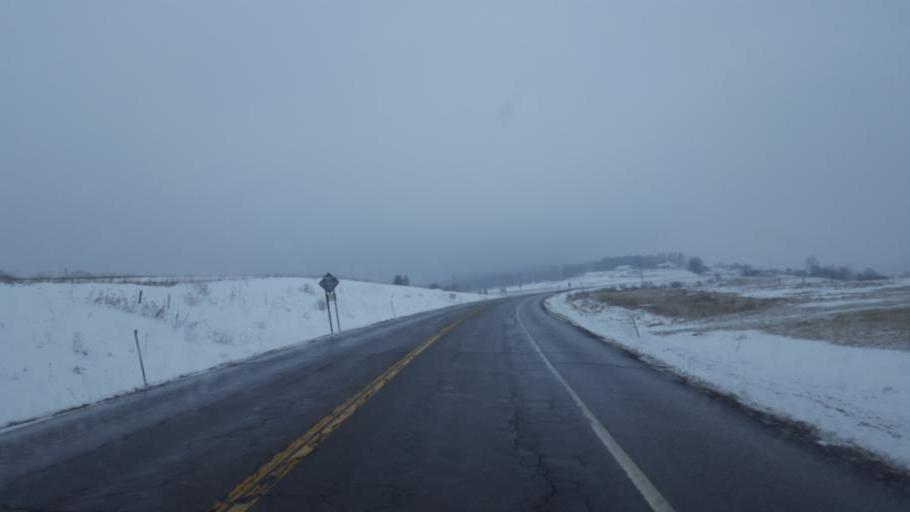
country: US
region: New York
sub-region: Steuben County
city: Canisteo
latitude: 42.1309
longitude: -77.5147
